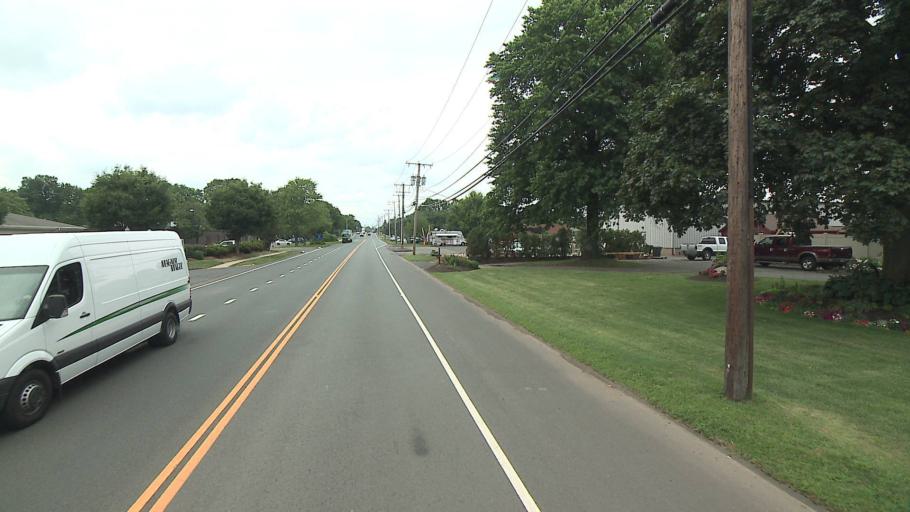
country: US
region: Connecticut
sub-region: Middlesex County
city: Cromwell
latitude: 41.6394
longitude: -72.6765
